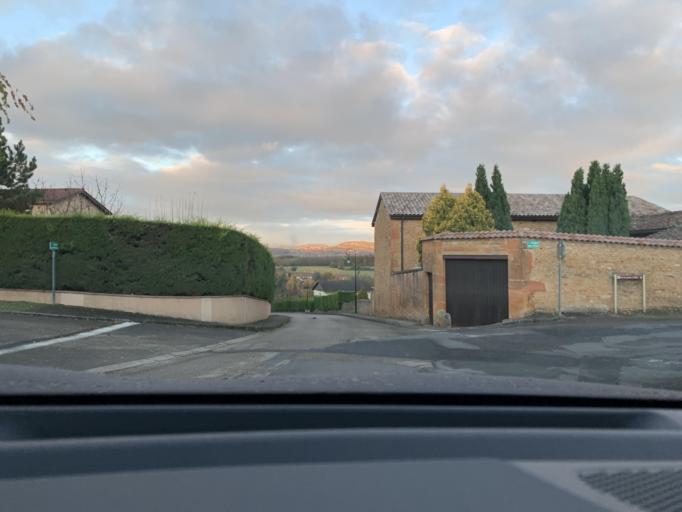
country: FR
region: Rhone-Alpes
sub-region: Departement du Rhone
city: Lucenay
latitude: 45.9161
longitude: 4.6776
